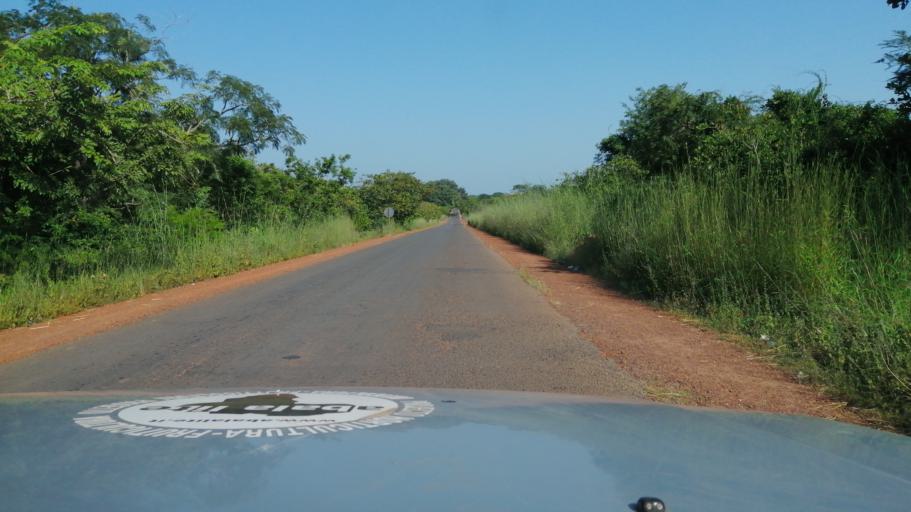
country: GW
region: Bissau
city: Bissau
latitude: 11.9589
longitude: -15.5334
